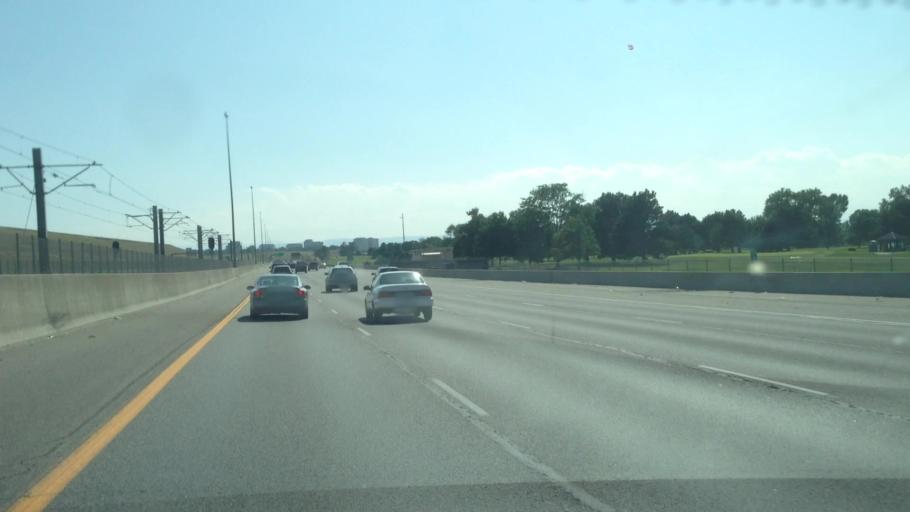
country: US
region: Colorado
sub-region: Arapahoe County
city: Centennial
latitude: 39.6527
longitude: -104.8584
